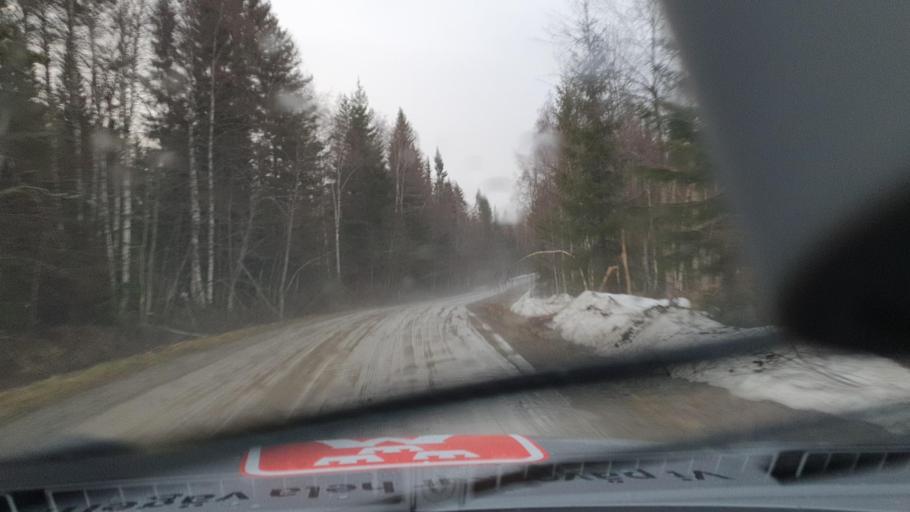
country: SE
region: Vaesternorrland
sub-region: OErnskoeldsviks Kommun
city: Bjasta
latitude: 63.2164
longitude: 18.2747
